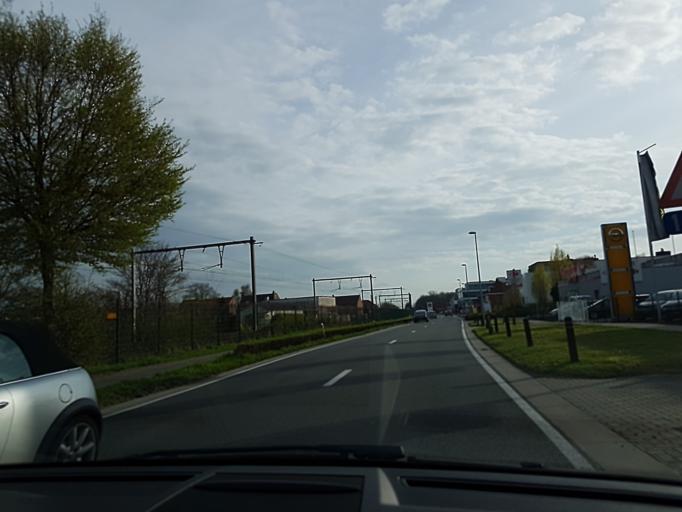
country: BE
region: Flanders
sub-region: Provincie West-Vlaanderen
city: Oostkamp
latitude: 51.1583
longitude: 3.1900
